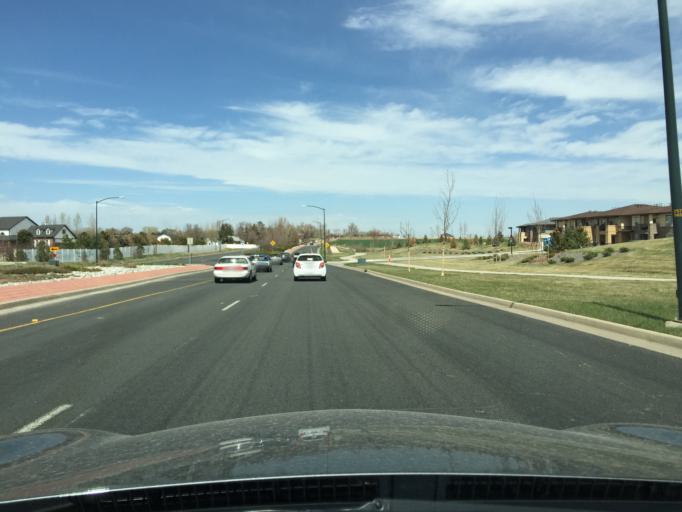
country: US
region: Colorado
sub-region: Adams County
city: Northglenn
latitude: 39.9659
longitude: -104.9966
